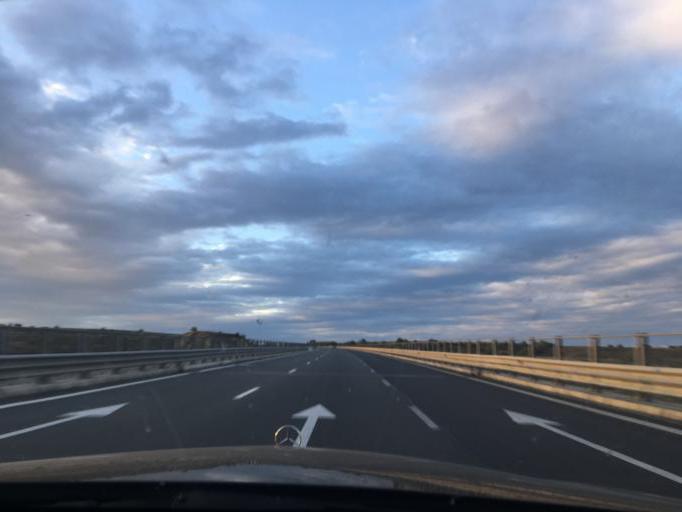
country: RO
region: Cluj
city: Turda
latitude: 46.5580
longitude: 23.7632
